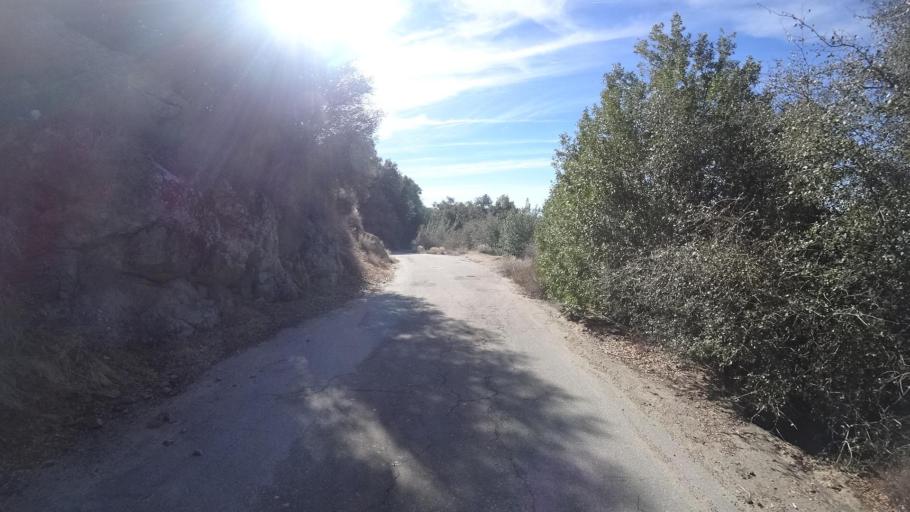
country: US
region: California
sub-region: Kern County
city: Bodfish
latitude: 35.4710
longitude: -118.6476
